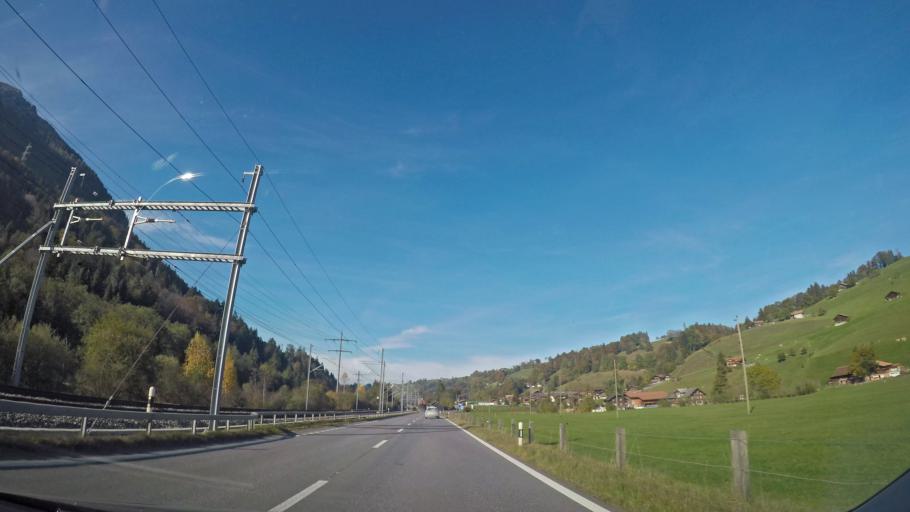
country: CH
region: Bern
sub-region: Frutigen-Niedersimmental District
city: Aeschi
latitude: 46.6335
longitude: 7.6916
